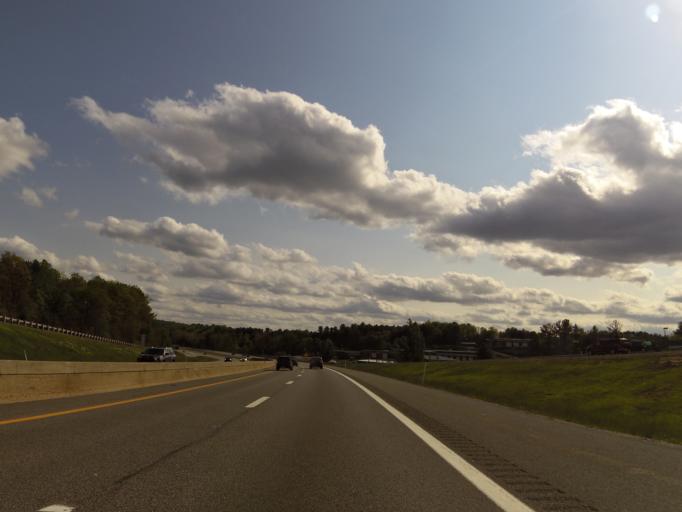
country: US
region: West Virginia
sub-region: Raleigh County
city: Mabscott
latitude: 37.7913
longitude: -81.2186
